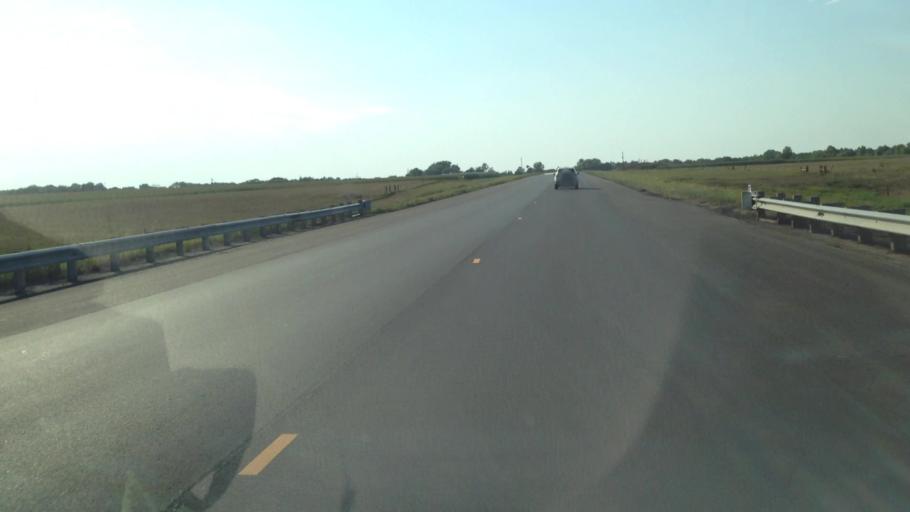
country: US
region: Kansas
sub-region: Franklin County
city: Ottawa
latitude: 38.4676
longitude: -95.2598
